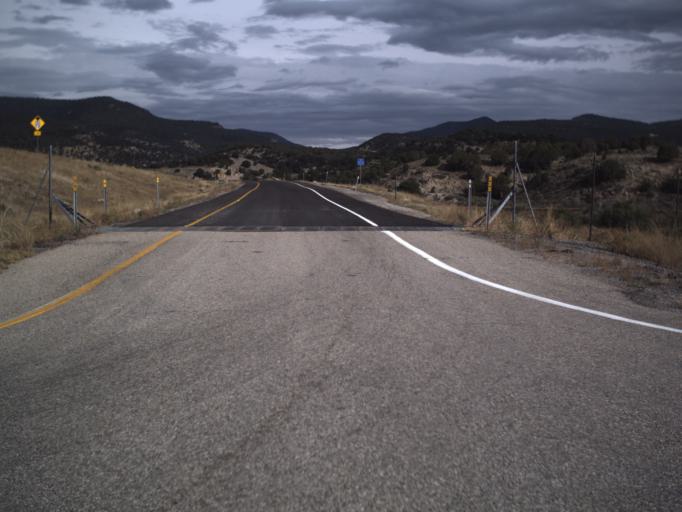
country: US
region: Utah
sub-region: Sevier County
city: Salina
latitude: 38.9159
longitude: -111.7402
